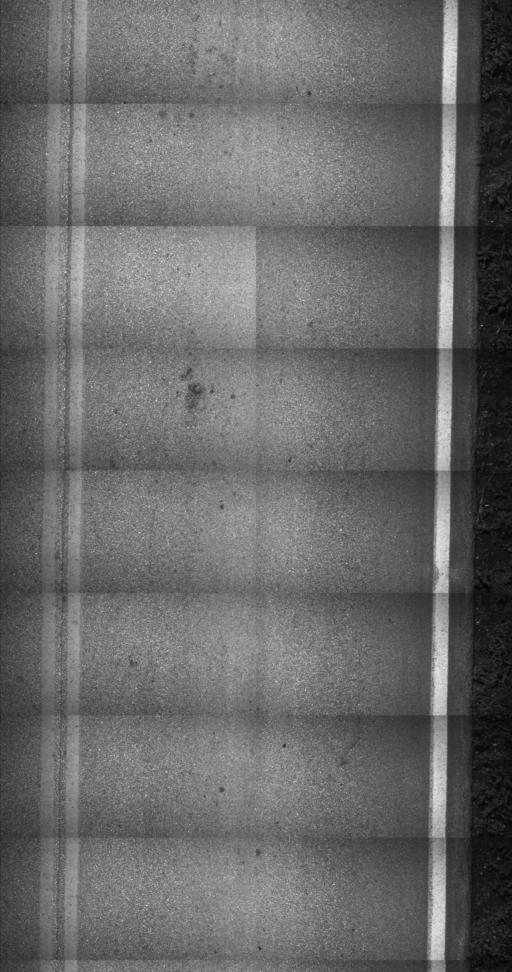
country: US
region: Vermont
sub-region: Rutland County
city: Poultney
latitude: 43.4934
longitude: -73.2375
